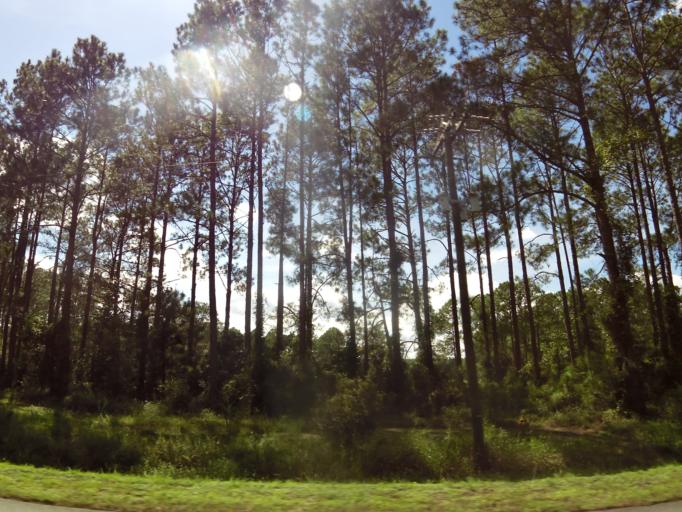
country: US
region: Georgia
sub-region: Clinch County
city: Homerville
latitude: 30.6953
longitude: -82.5652
